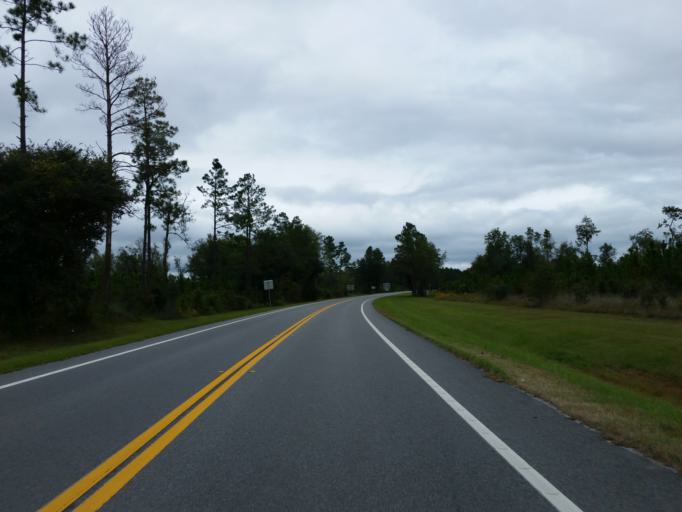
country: US
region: Georgia
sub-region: Echols County
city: Statenville
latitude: 30.6121
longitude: -83.0223
